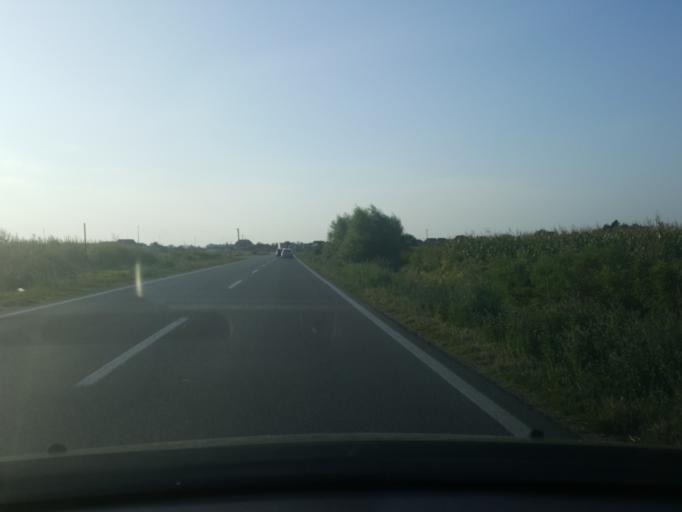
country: RS
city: Majur
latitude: 44.7699
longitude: 19.6269
